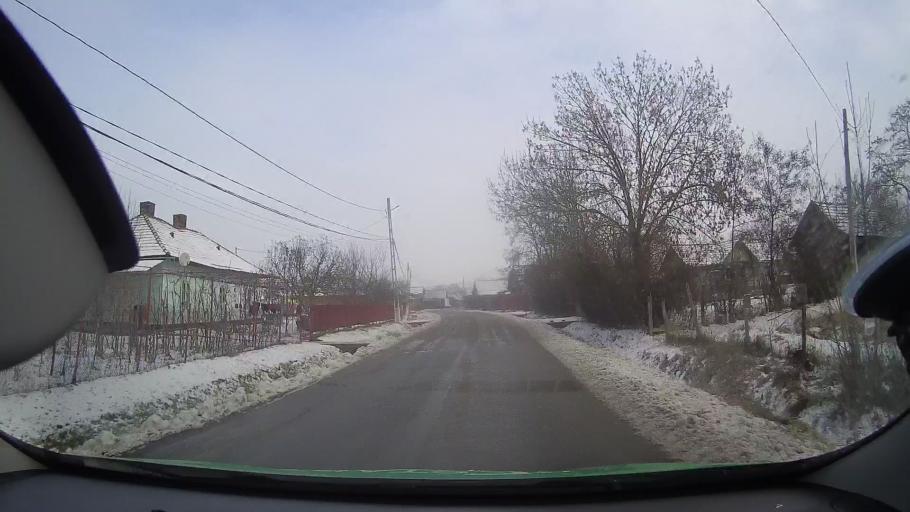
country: RO
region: Mures
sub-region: Comuna Chetani
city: Chetani
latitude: 46.4277
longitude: 23.9997
